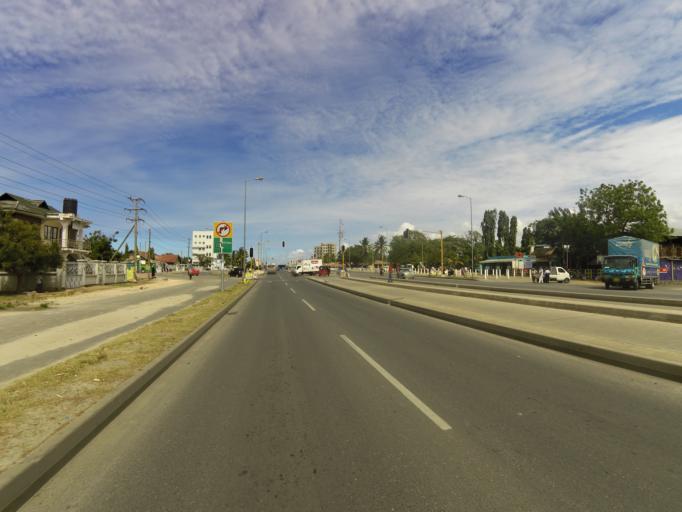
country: TZ
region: Dar es Salaam
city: Magomeni
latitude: -6.8048
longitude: 39.2509
